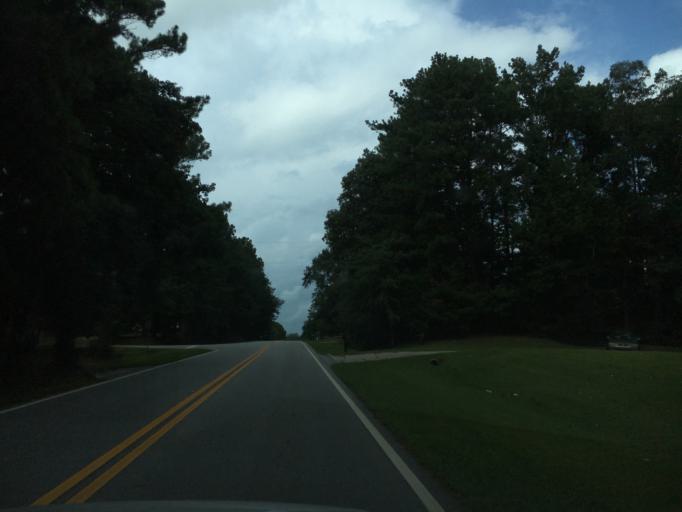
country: US
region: Georgia
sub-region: Rockdale County
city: Lakeview Estates
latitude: 33.7256
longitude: -84.0190
